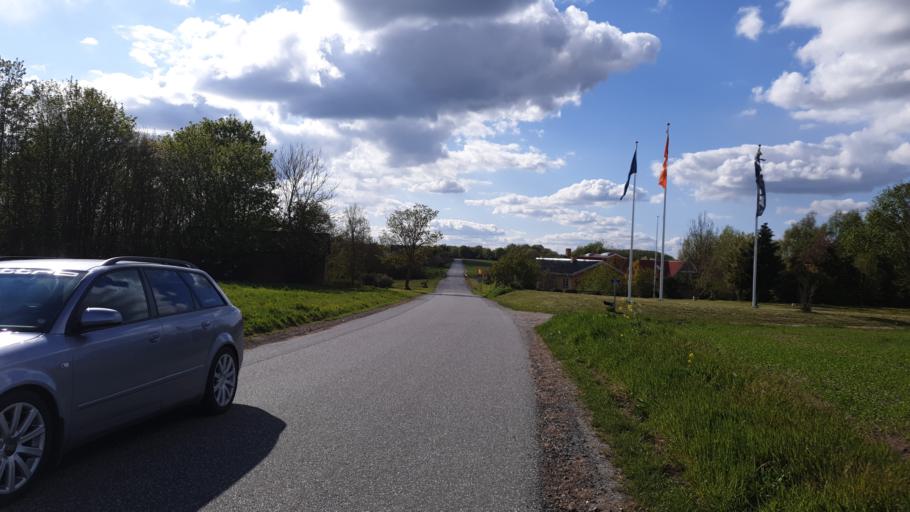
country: DK
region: Central Jutland
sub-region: Hedensted Kommune
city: Hedensted
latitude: 55.8099
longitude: 9.6722
